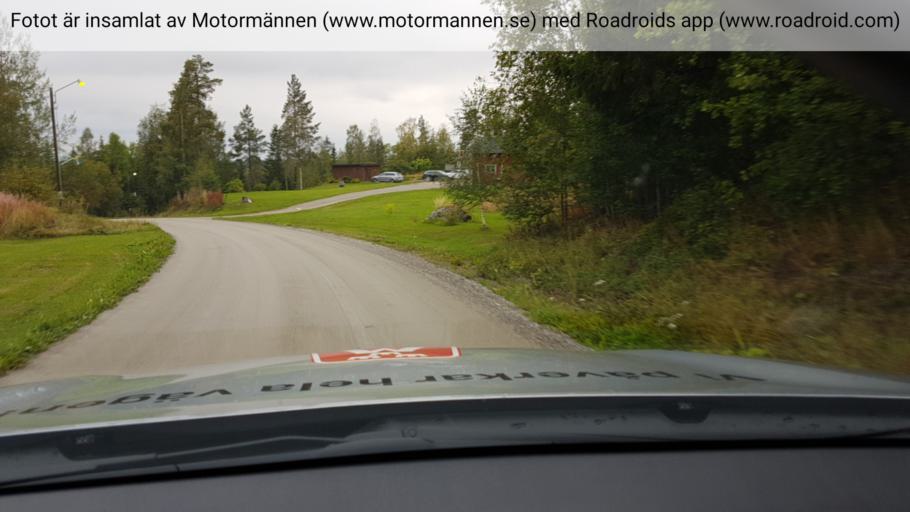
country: SE
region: Jaemtland
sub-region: Braecke Kommun
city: Braecke
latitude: 62.7688
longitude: 15.4900
